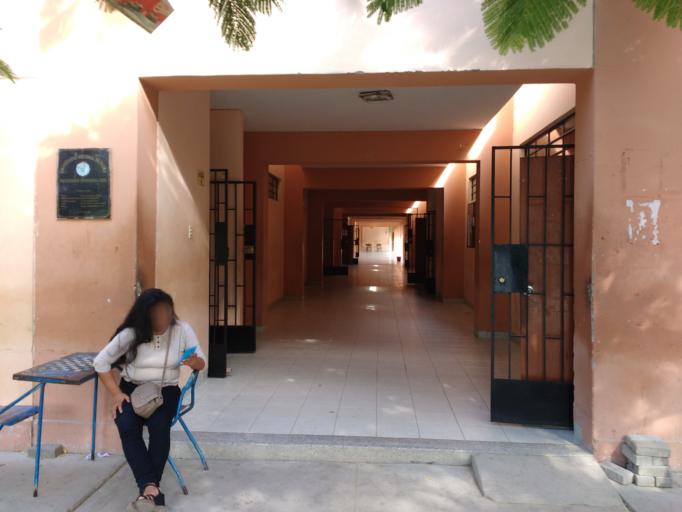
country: PE
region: Piura
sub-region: Provincia de Piura
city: Piura
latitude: -5.1804
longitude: -80.6216
